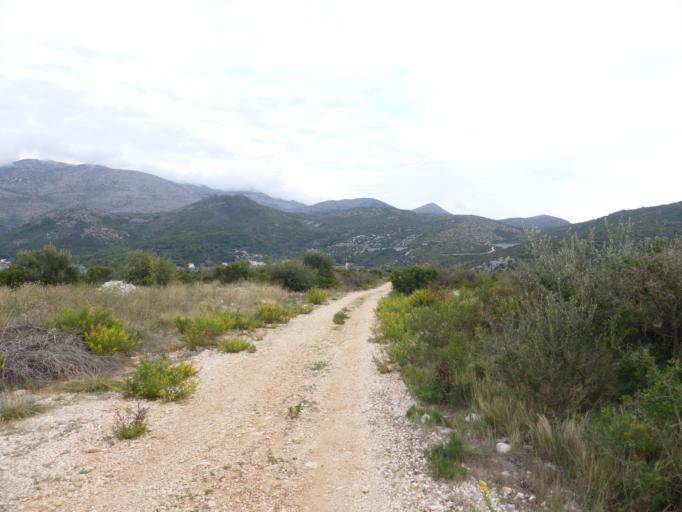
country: HR
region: Dubrovacko-Neretvanska
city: Podgora
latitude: 42.7783
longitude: 17.8674
